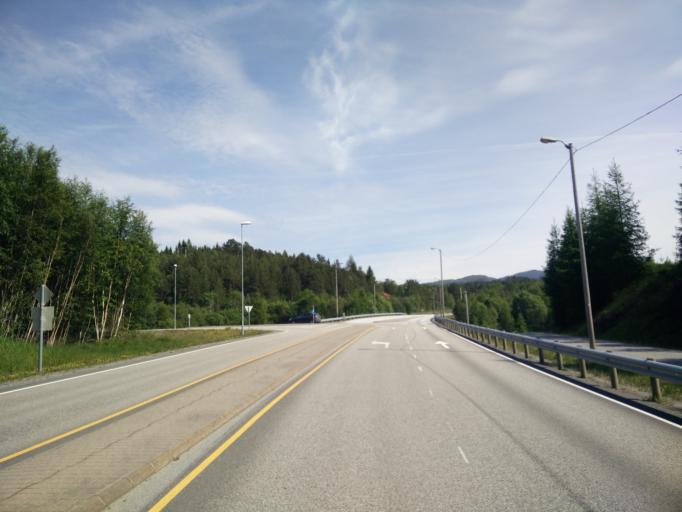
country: NO
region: More og Romsdal
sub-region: Kristiansund
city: Rensvik
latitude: 63.0118
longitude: 7.9994
